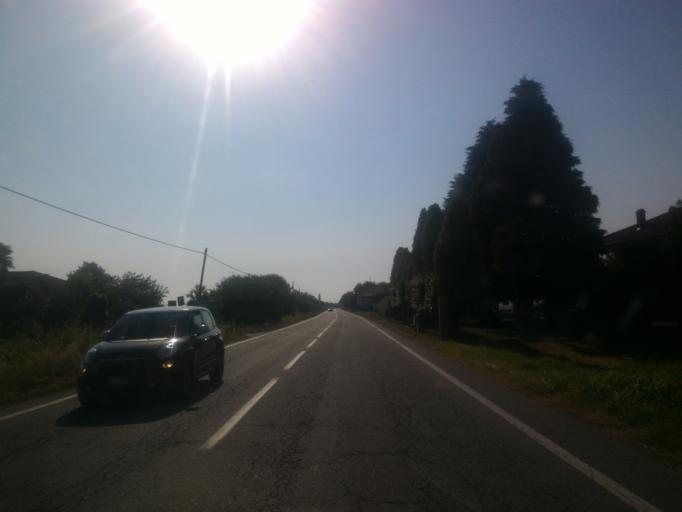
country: IT
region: Piedmont
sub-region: Provincia di Torino
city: Buriasco
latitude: 44.8752
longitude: 7.3945
